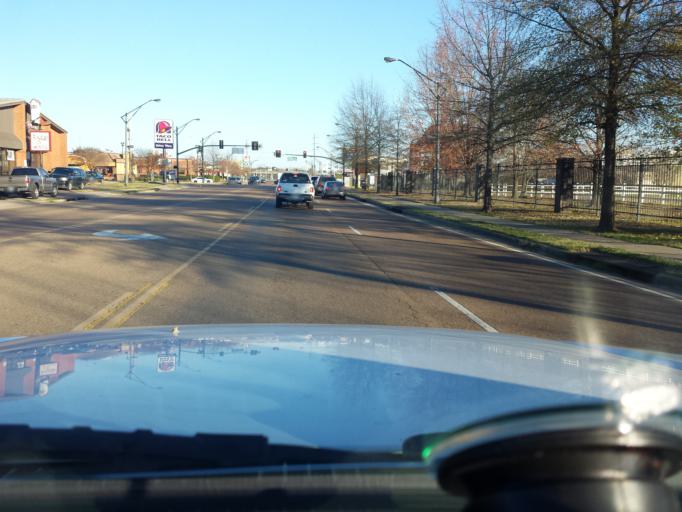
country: US
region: Mississippi
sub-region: Hinds County
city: Jackson
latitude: 32.3037
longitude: -90.1729
